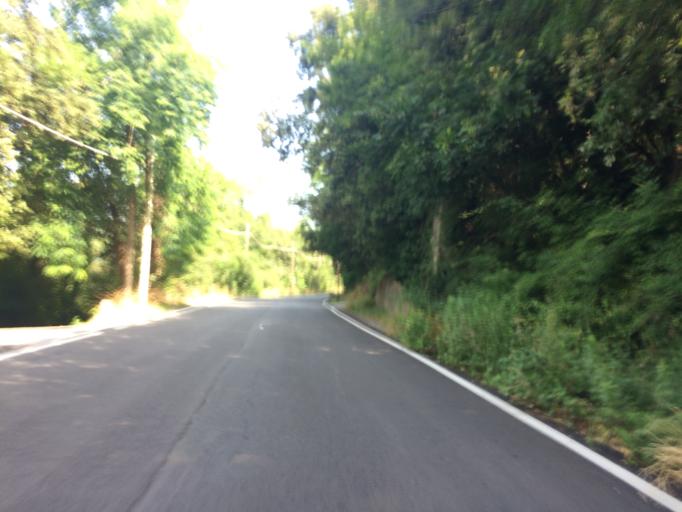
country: IT
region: Liguria
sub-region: Provincia di Savona
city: Varazze
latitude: 44.3800
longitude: 8.5682
